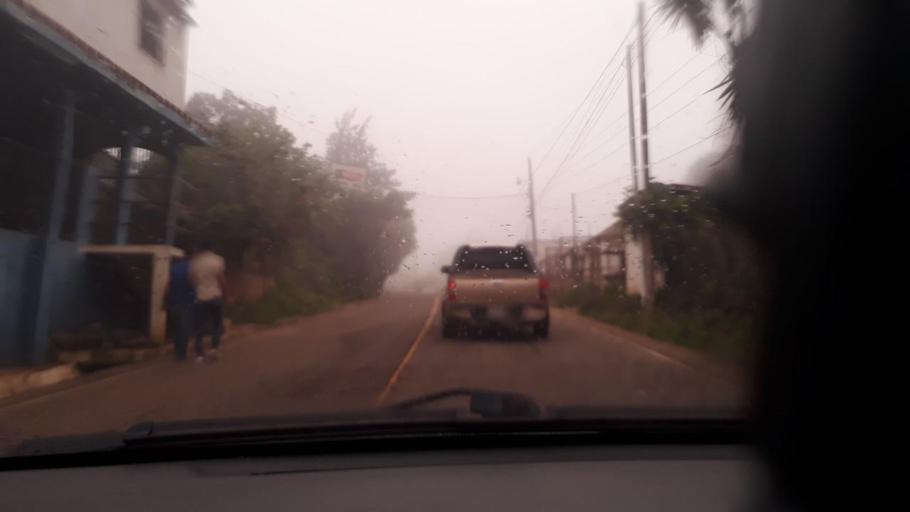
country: GT
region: Jutiapa
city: Jalpatagua
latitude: 14.1810
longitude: -90.0222
